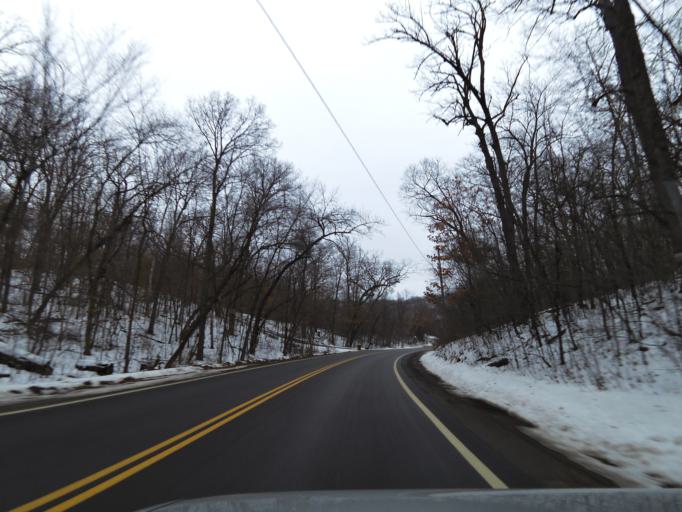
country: US
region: Minnesota
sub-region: Washington County
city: Afton
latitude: 44.8307
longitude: -92.7991
